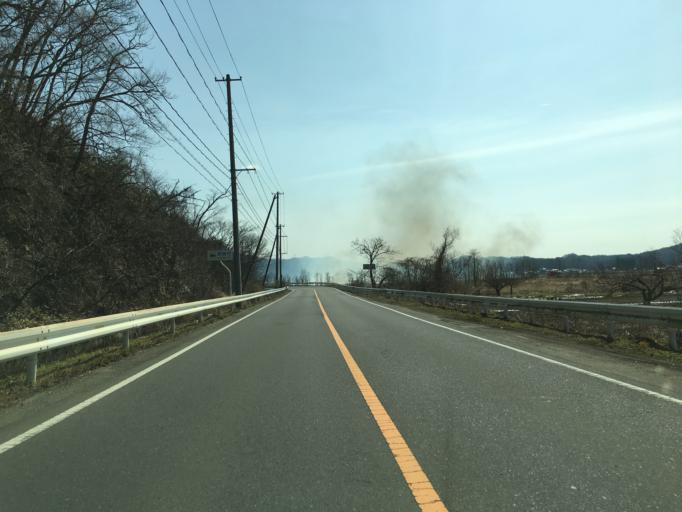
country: JP
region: Fukushima
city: Ishikawa
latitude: 37.1306
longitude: 140.2931
